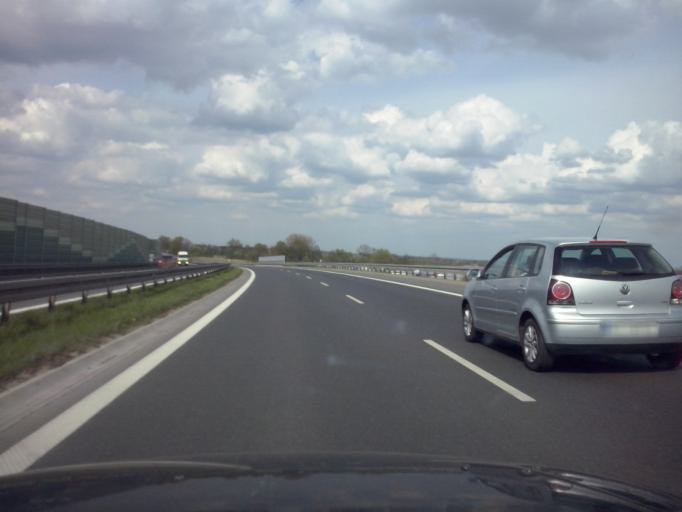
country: PL
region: Subcarpathian Voivodeship
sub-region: Powiat rzeszowski
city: Trzebownisko
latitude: 50.0667
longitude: 22.0541
